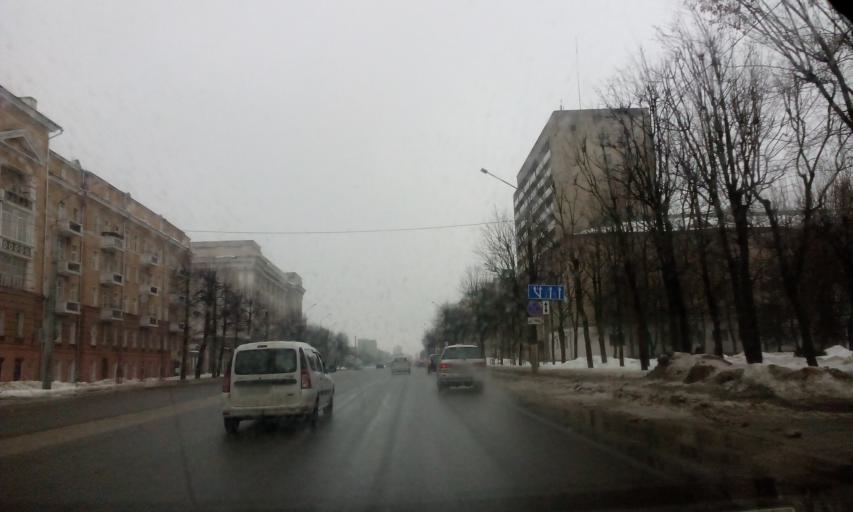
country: BY
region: Mogilev
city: Mahilyow
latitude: 53.9059
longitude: 30.3450
